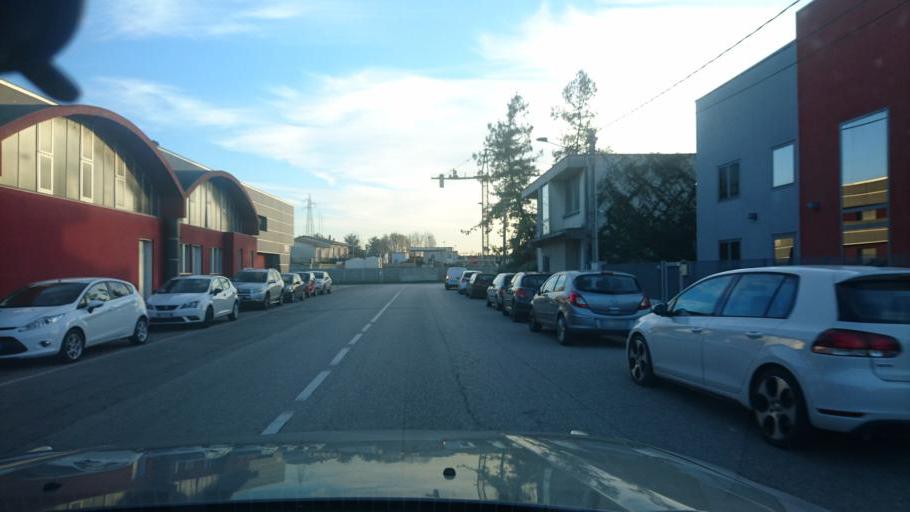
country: IT
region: Veneto
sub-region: Provincia di Padova
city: Noventa
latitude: 45.4126
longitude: 11.9364
